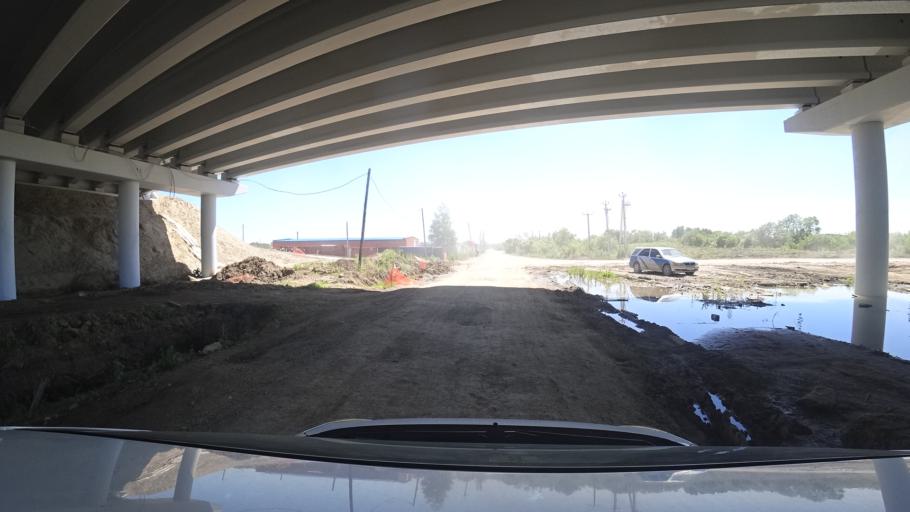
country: RU
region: Khabarovsk Krai
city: Topolevo
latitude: 48.4818
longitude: 135.1745
